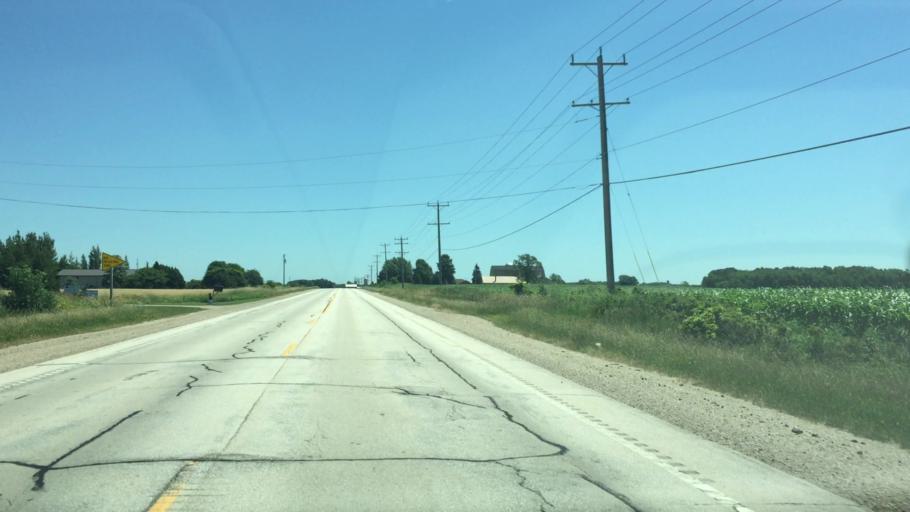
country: US
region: Wisconsin
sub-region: Calumet County
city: Sherwood
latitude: 44.1405
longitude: -88.2179
